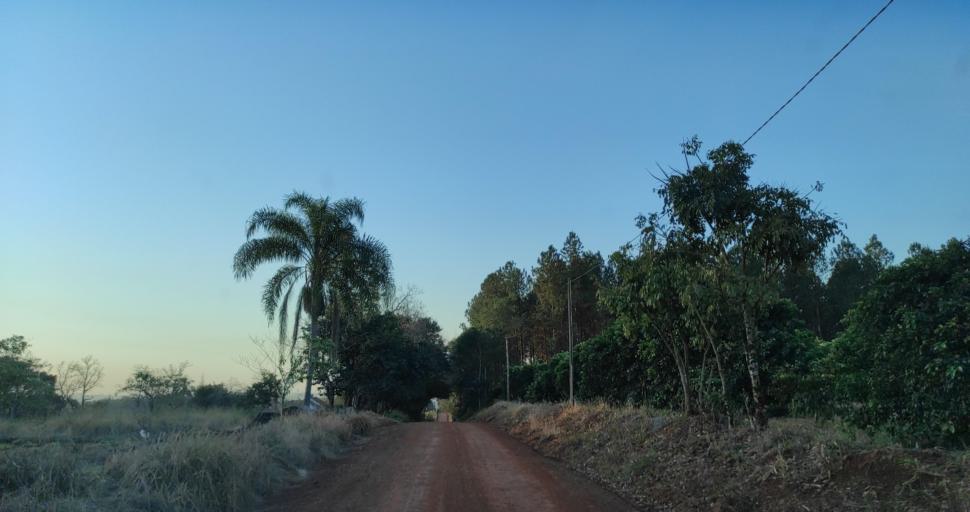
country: AR
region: Misiones
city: Capiovi
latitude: -26.8753
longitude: -55.1078
